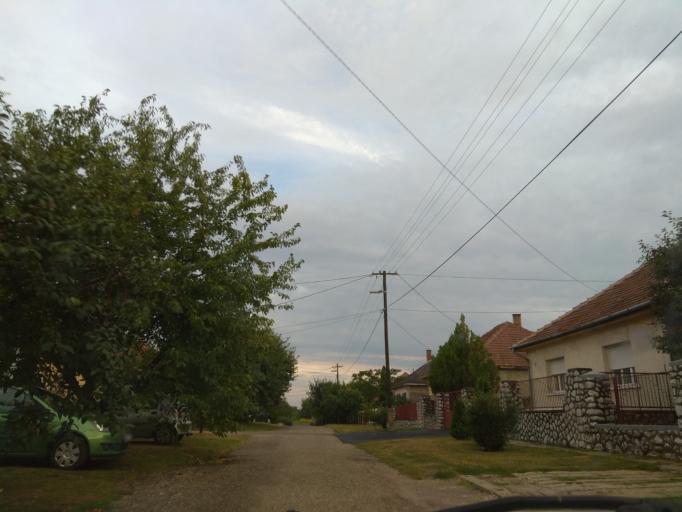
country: HU
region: Borsod-Abauj-Zemplen
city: Miskolc
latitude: 48.0748
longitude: 20.8233
